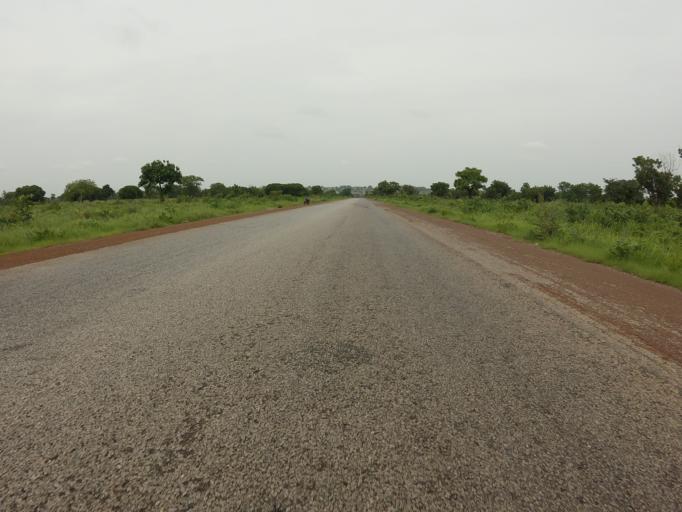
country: GH
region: Northern
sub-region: Yendi
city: Yendi
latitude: 9.4129
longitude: -0.0104
